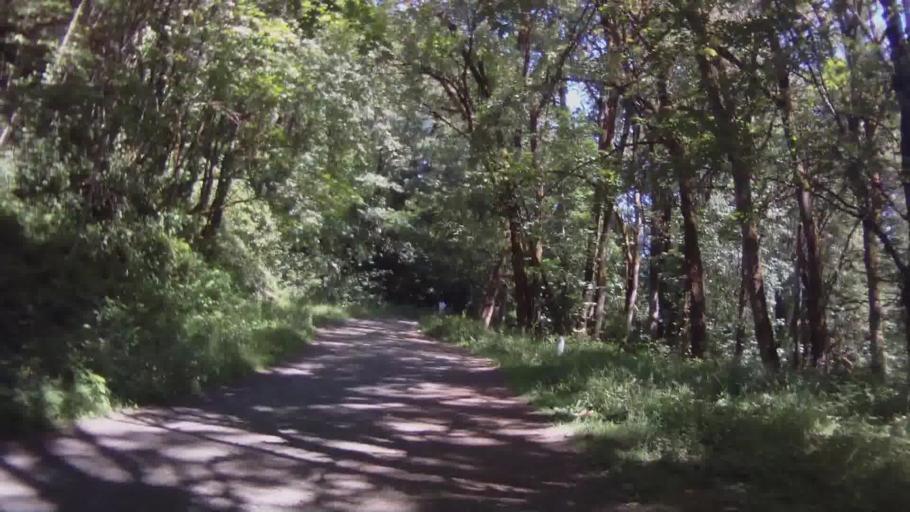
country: US
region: Oregon
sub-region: Washington County
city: West Haven-Sylvan
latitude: 45.5427
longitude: -122.7266
